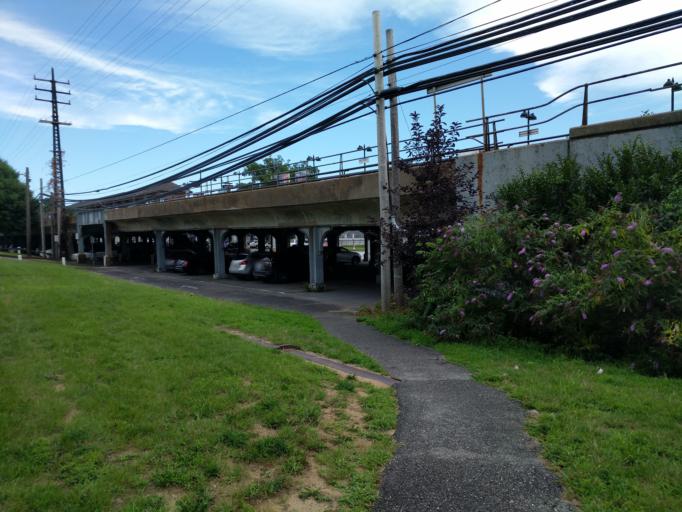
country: US
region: New York
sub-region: Nassau County
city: Valley Stream
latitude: 40.6621
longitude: -73.7059
